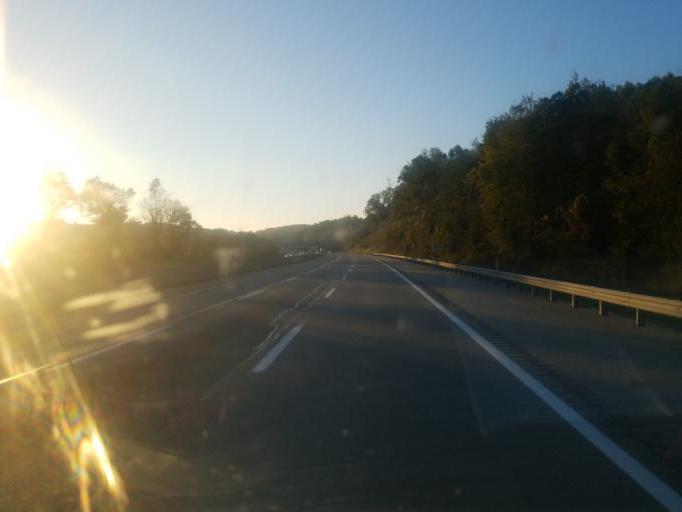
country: US
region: Pennsylvania
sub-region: Beaver County
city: Big Beaver
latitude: 40.8460
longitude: -80.3921
